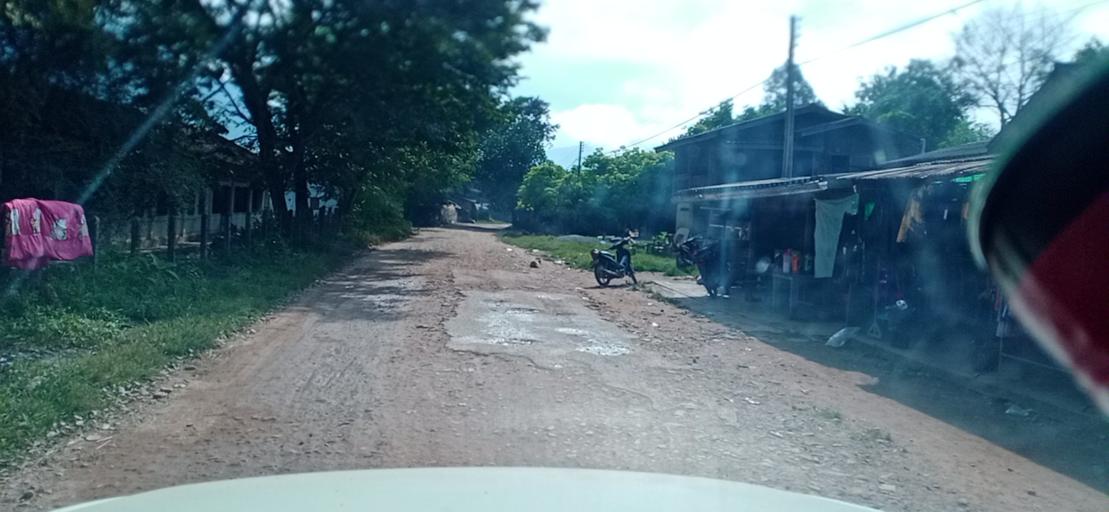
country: TH
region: Changwat Bueng Kan
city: Pak Khat
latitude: 18.6776
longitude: 103.1911
